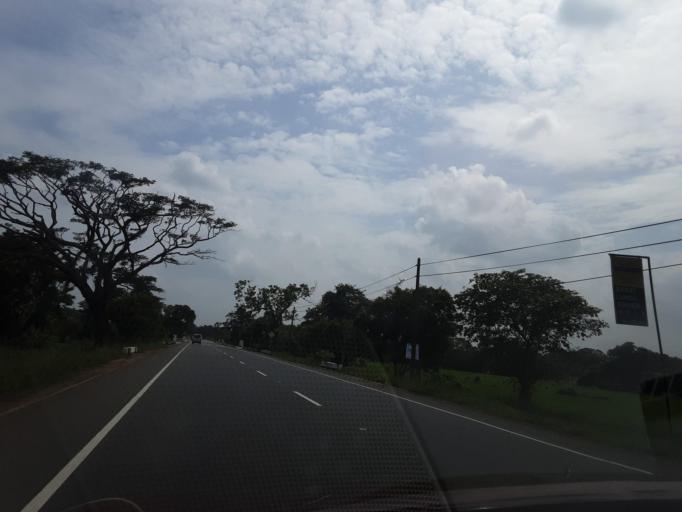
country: LK
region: North Central
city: Anuradhapura
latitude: 8.5098
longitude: 80.5062
